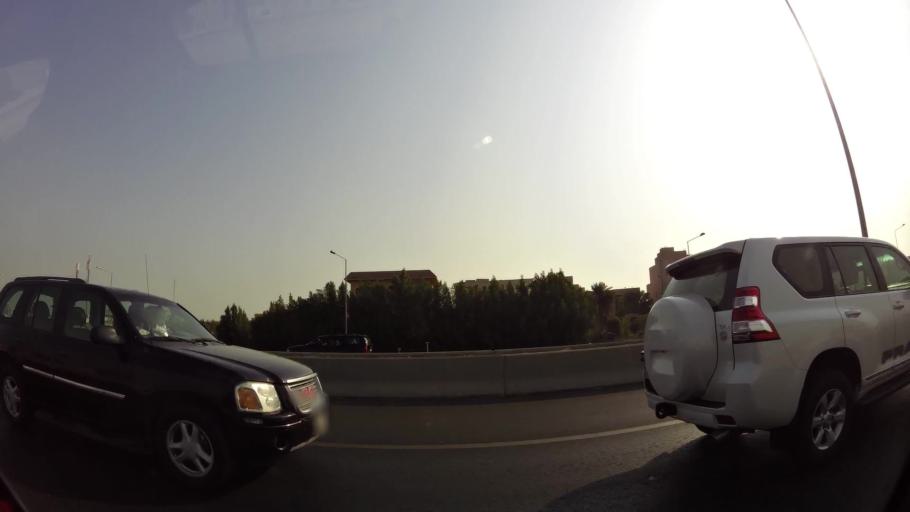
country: KW
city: Al Funaytis
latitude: 29.2250
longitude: 48.0993
